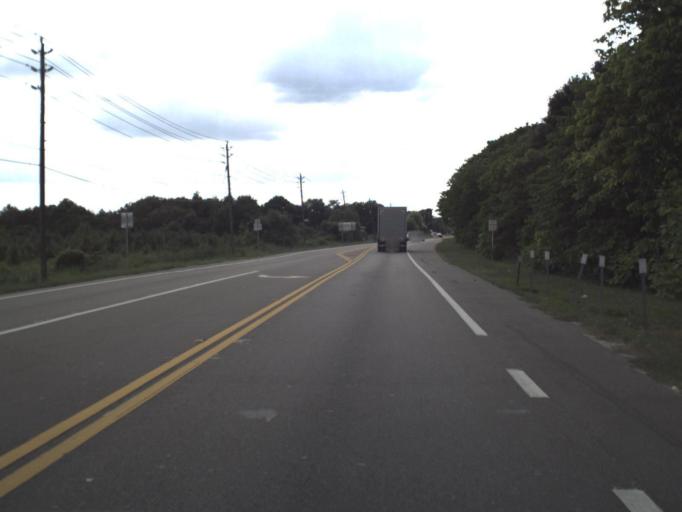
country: US
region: Florida
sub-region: Polk County
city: Winston
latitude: 28.0349
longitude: -82.0201
